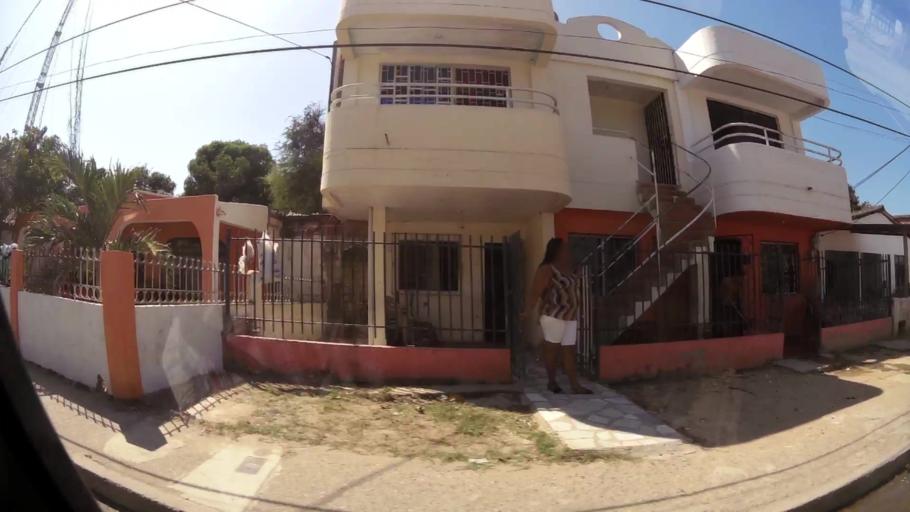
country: CO
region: Bolivar
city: Cartagena
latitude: 10.4262
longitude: -75.5159
